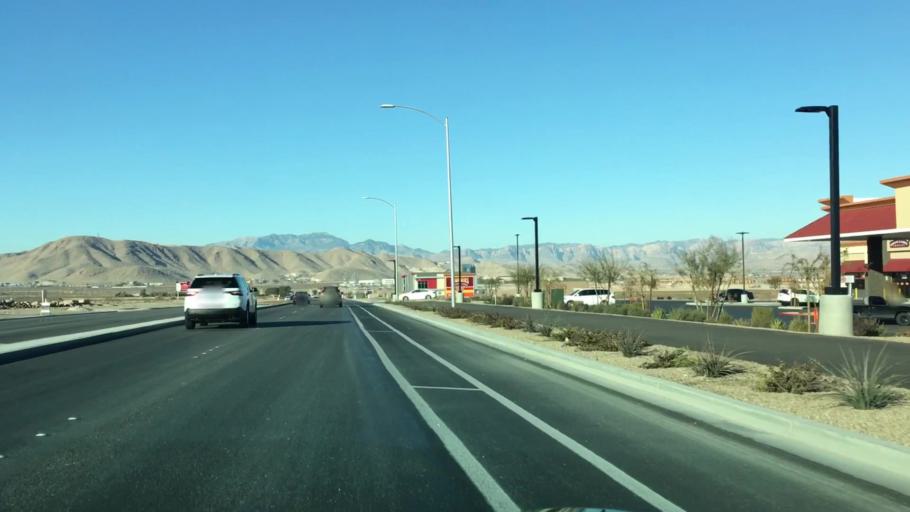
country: US
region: Nevada
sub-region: Clark County
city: Enterprise
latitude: 35.9599
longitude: -115.1402
